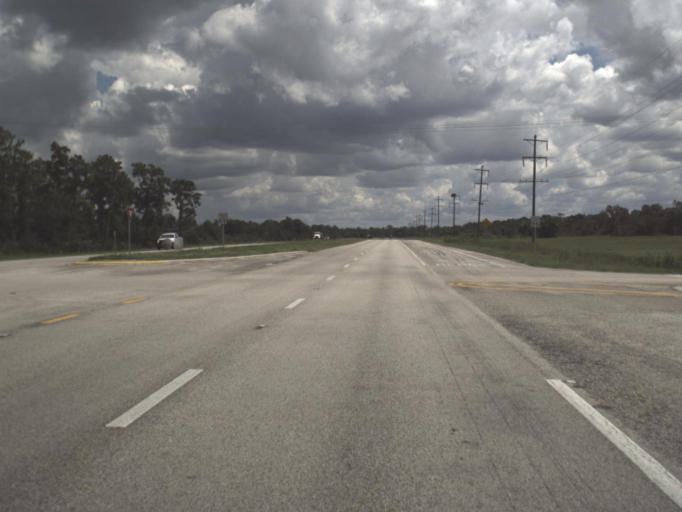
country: US
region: Florida
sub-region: Polk County
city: Babson Park
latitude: 27.8135
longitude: -81.3254
